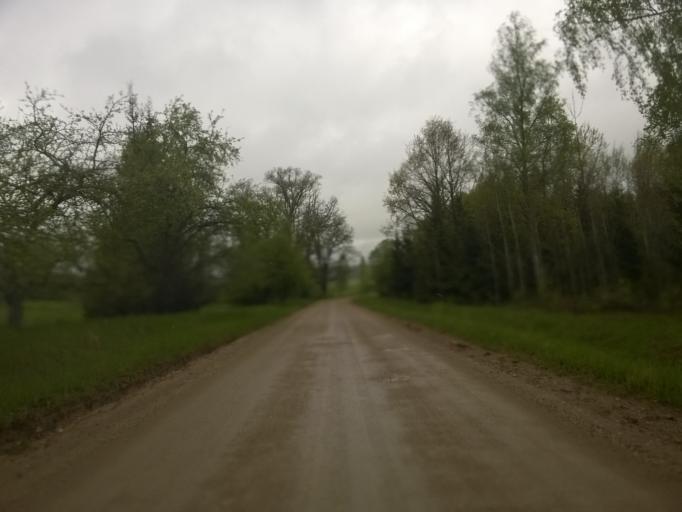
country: LV
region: Amatas Novads
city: Drabesi
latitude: 57.2212
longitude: 25.1961
